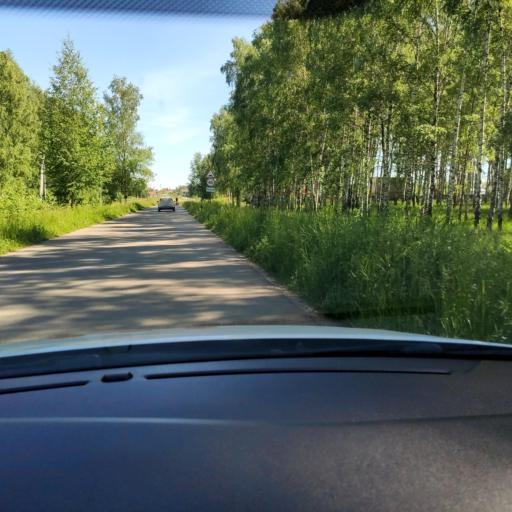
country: RU
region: Tatarstan
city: Staroye Arakchino
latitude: 55.8884
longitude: 49.0347
